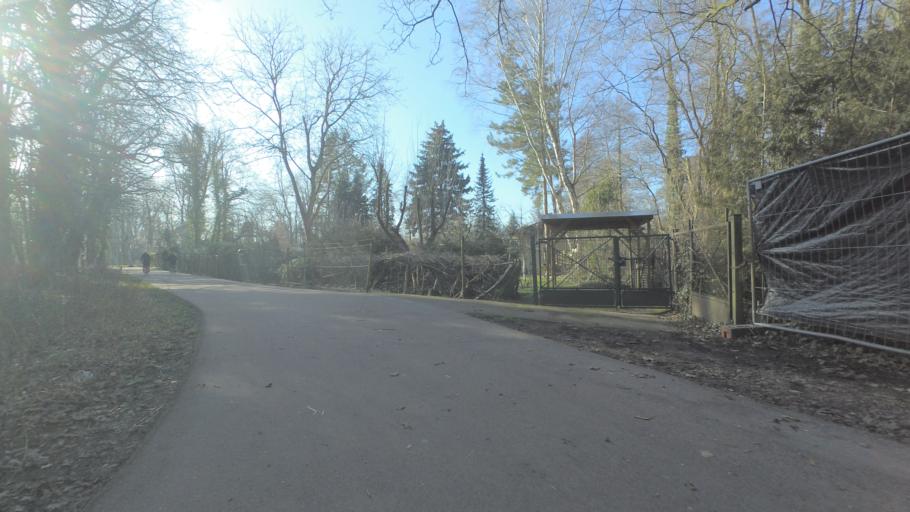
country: DE
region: Brandenburg
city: Luckenwalde
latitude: 52.0831
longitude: 13.1743
